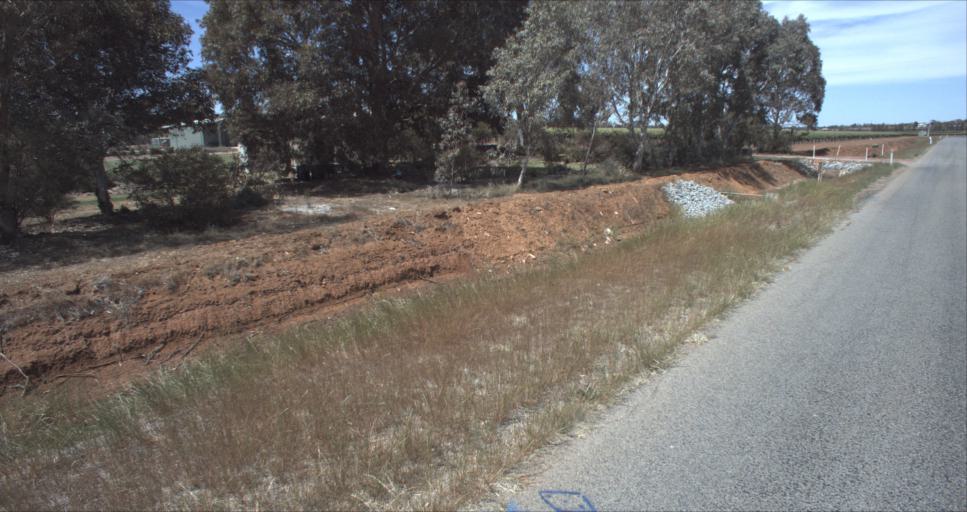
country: AU
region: New South Wales
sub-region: Leeton
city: Leeton
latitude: -34.5600
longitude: 146.4530
